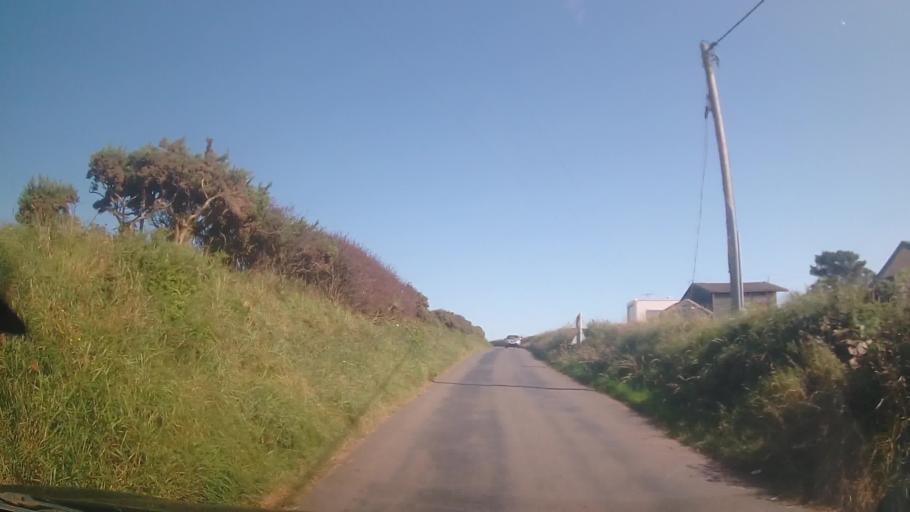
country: GB
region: Wales
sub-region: Pembrokeshire
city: Llanrhian
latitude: 51.9298
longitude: -5.1935
